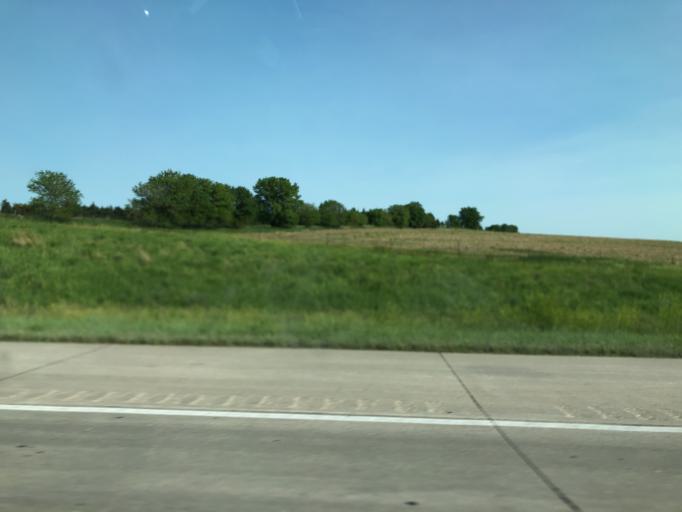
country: US
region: Nebraska
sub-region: Saunders County
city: Ashland
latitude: 40.9976
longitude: -96.3379
